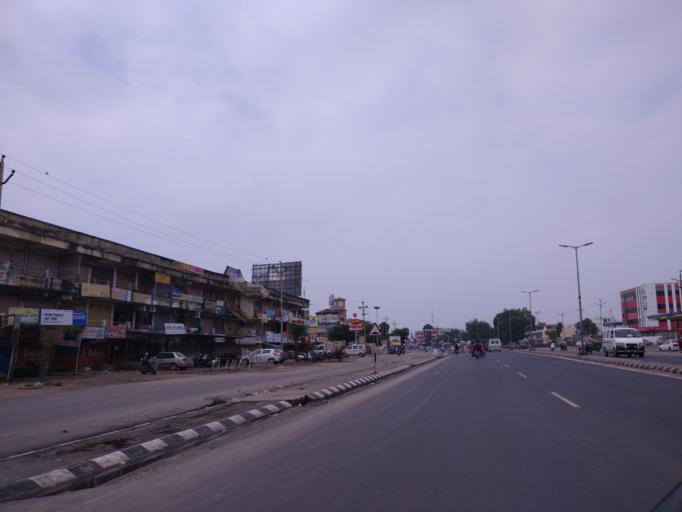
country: IN
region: Gujarat
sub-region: Mahesana
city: Visnagar
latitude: 23.5872
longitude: 72.3759
